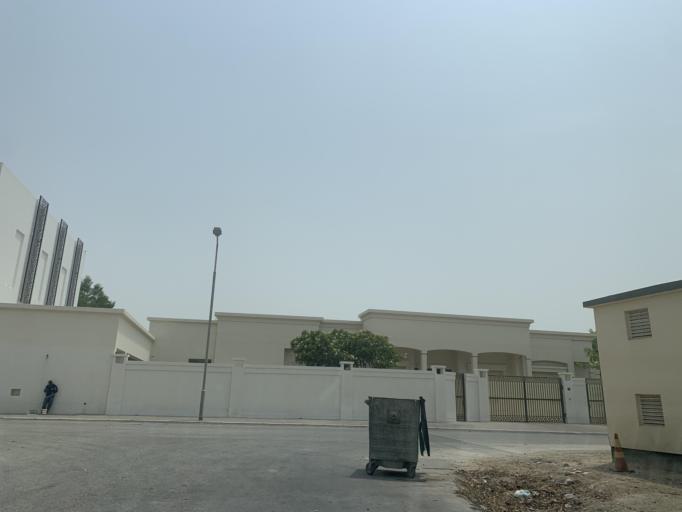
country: BH
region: Central Governorate
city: Madinat Hamad
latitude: 26.1607
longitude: 50.4787
